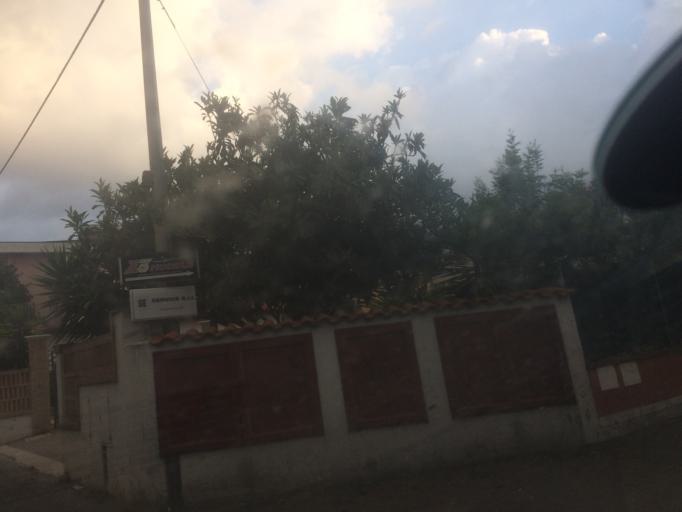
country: IT
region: Tuscany
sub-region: Provincia di Massa-Carrara
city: Massa
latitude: 44.0201
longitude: 10.0922
